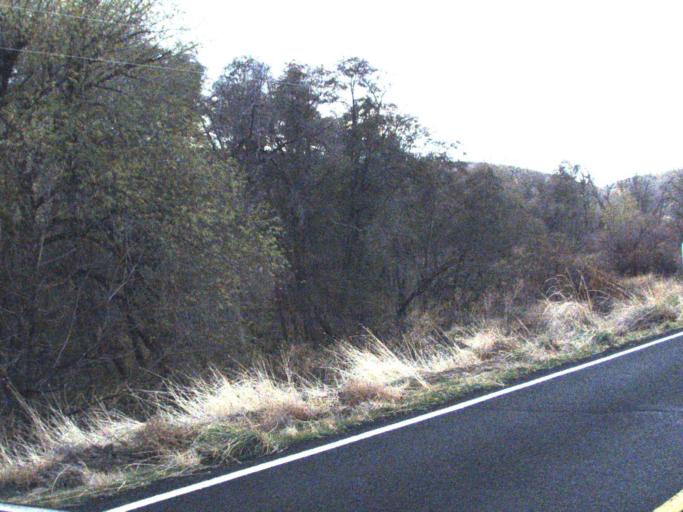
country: US
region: Washington
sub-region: Columbia County
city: Dayton
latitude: 46.5067
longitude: -118.0468
